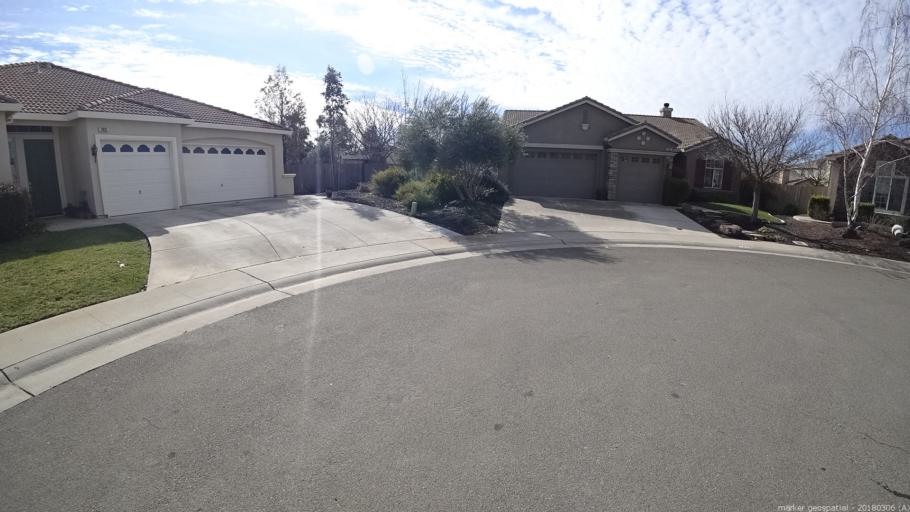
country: US
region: California
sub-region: Sacramento County
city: Vineyard
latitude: 38.4727
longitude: -121.3134
